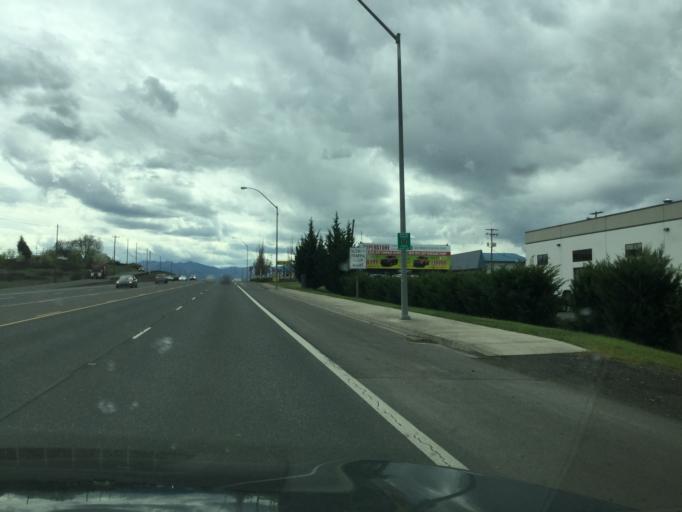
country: US
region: Oregon
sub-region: Jackson County
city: White City
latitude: 42.3866
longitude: -122.8561
